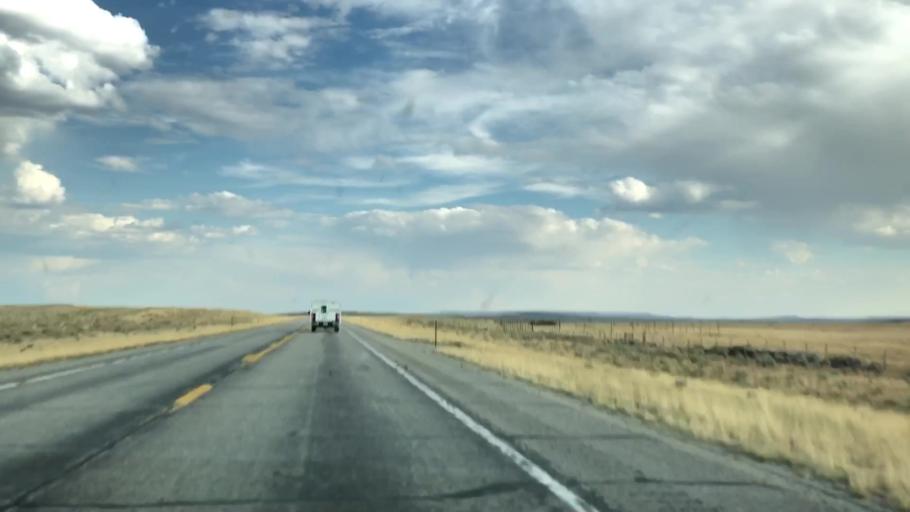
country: US
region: Wyoming
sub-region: Sublette County
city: Pinedale
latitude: 43.0398
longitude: -110.1384
